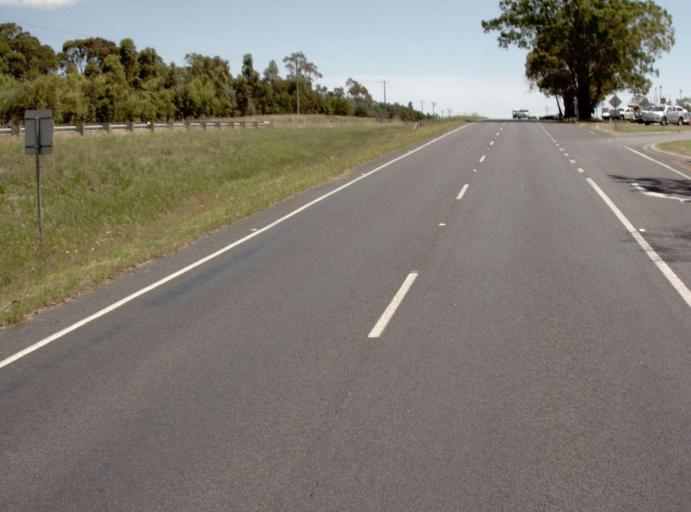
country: AU
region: Victoria
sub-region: Latrobe
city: Traralgon
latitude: -38.2082
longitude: 146.4980
